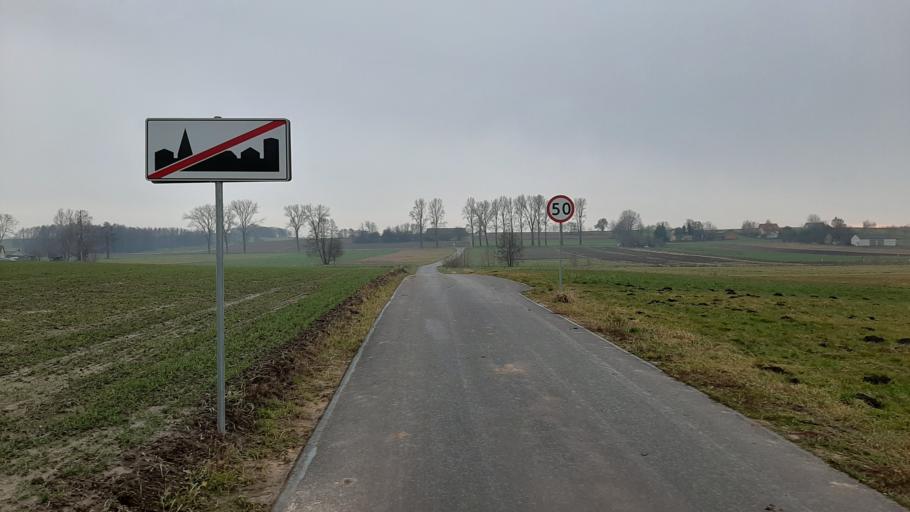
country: PL
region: Lublin Voivodeship
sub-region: Powiat lubelski
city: Jastkow
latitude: 51.3489
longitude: 22.3923
